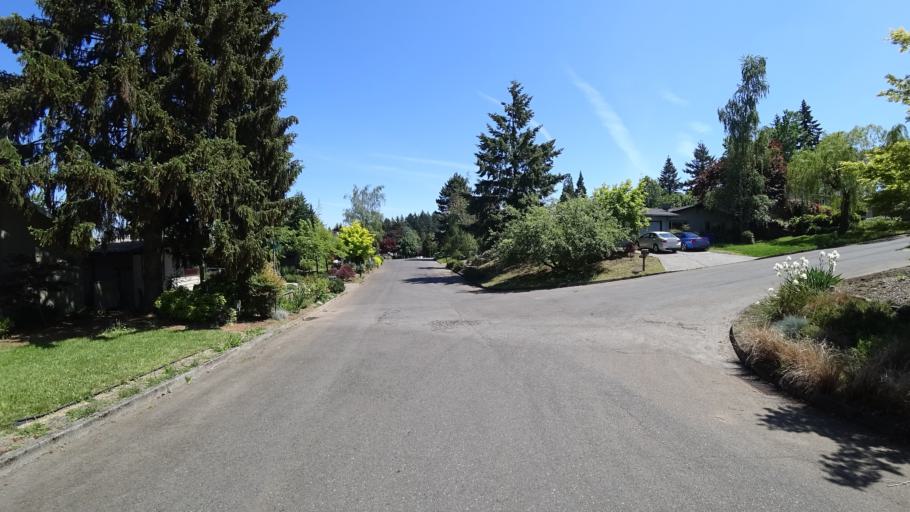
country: US
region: Oregon
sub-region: Washington County
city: Metzger
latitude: 45.4545
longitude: -122.7094
